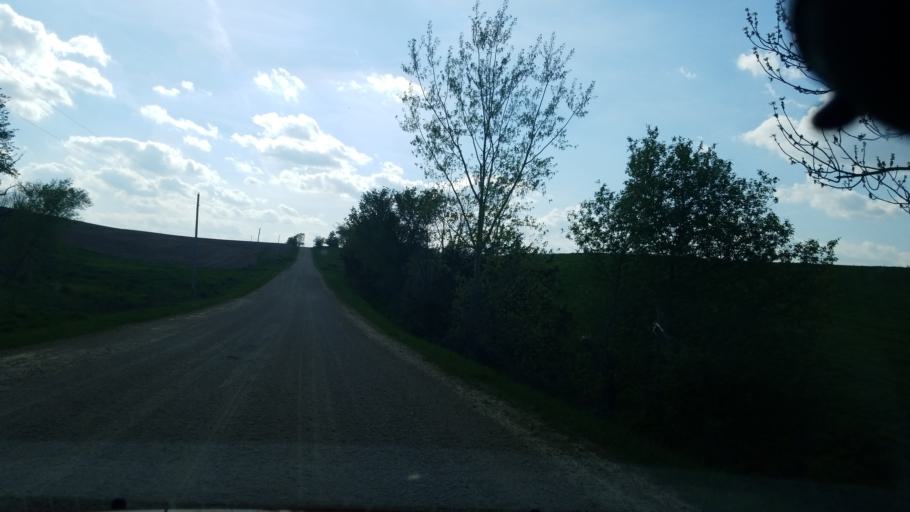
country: US
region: Iowa
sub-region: Jackson County
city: Maquoketa
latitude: 42.2150
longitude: -90.7058
